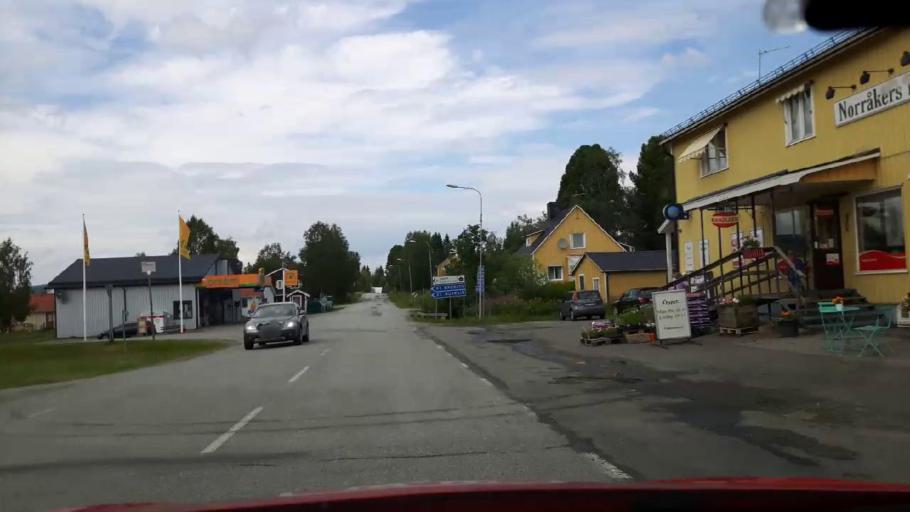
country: SE
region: Jaemtland
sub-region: Stroemsunds Kommun
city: Stroemsund
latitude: 64.4352
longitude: 15.5939
